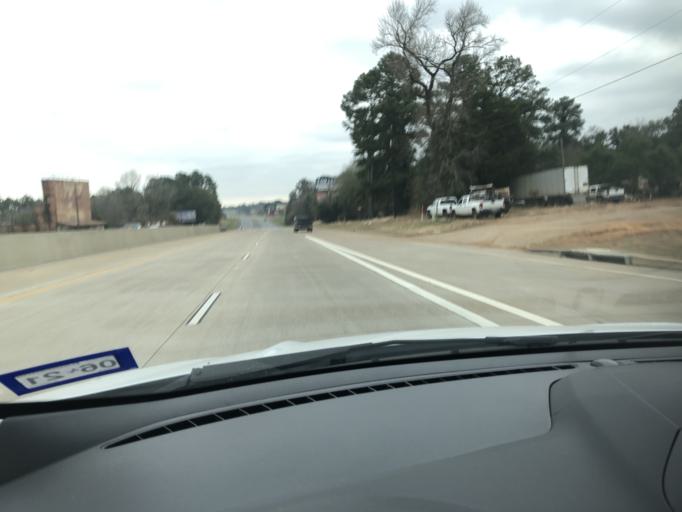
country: US
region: Texas
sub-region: Angelina County
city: Redland
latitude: 31.4021
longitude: -94.7195
